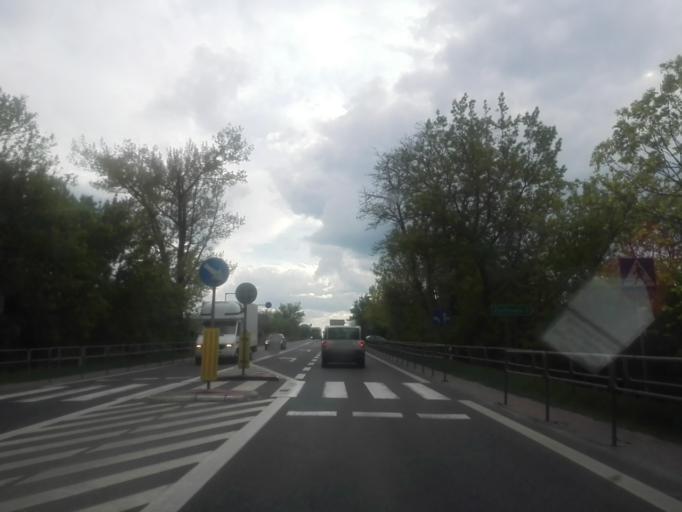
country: PL
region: Podlasie
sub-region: Powiat zambrowski
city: Szumowo
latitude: 52.8710
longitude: 22.0216
